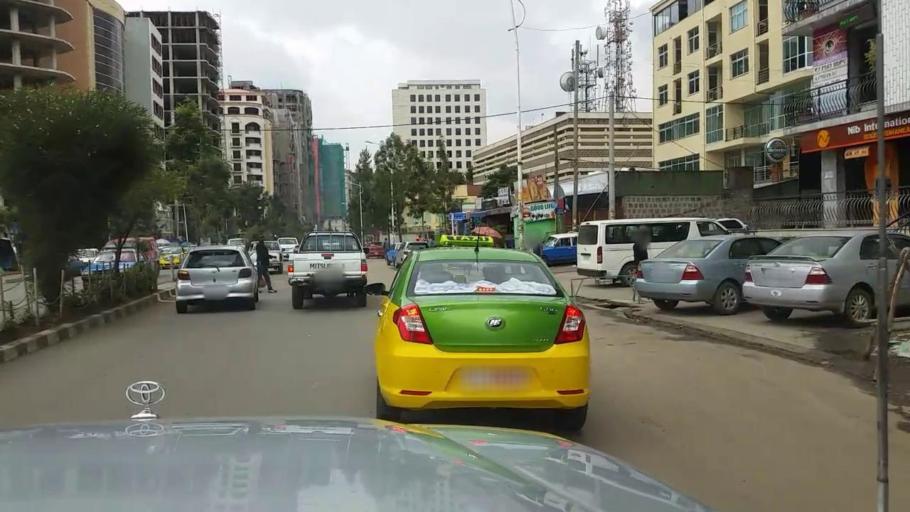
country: ET
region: Adis Abeba
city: Addis Ababa
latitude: 8.9992
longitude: 38.7851
